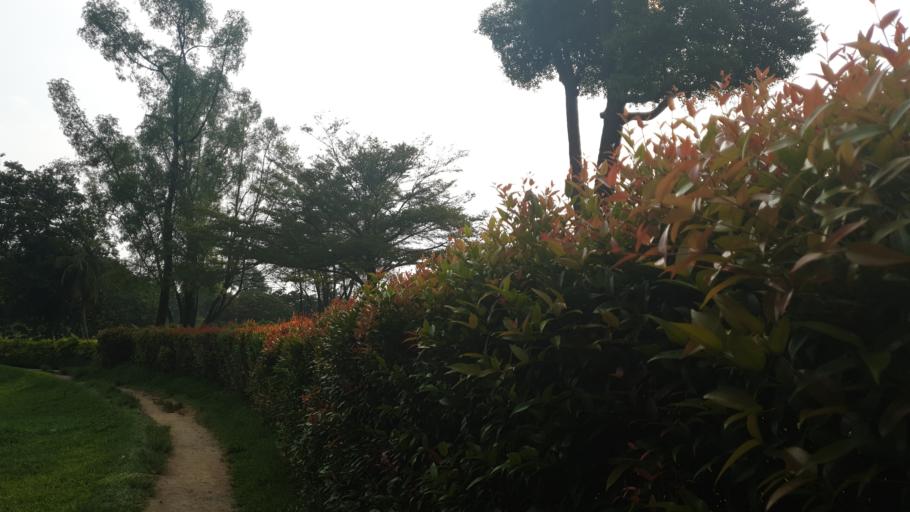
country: SG
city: Singapore
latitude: 1.3456
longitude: 103.8131
